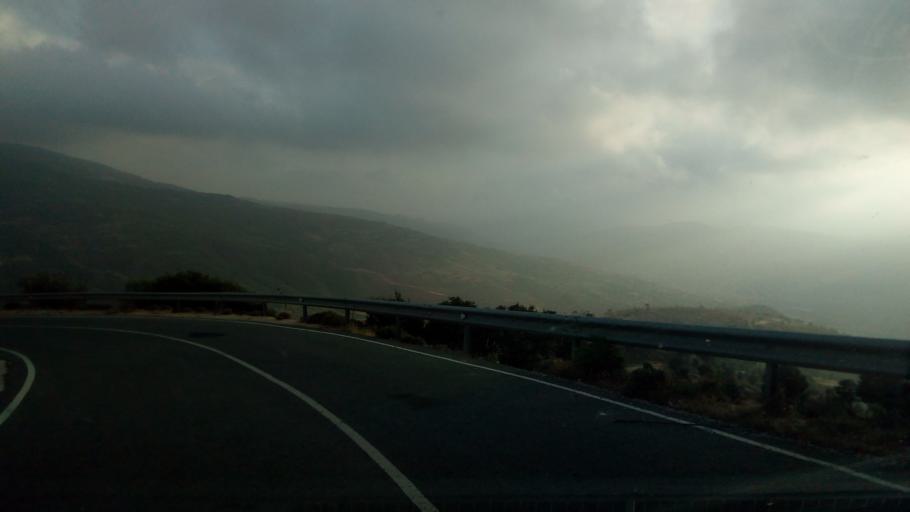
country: CY
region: Limassol
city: Pachna
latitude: 34.8404
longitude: 32.6725
